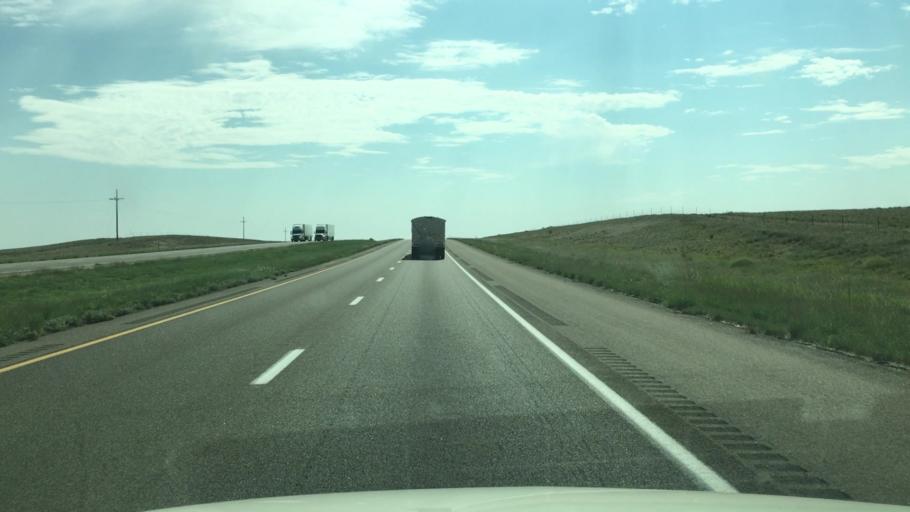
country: US
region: New Mexico
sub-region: Guadalupe County
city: Santa Rosa
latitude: 34.9820
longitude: -105.1033
